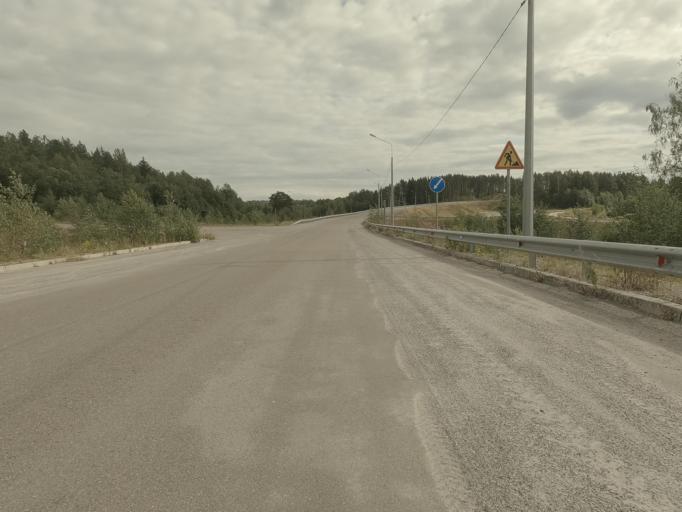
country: RU
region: Leningrad
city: Kamennogorsk
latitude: 60.9657
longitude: 29.1402
